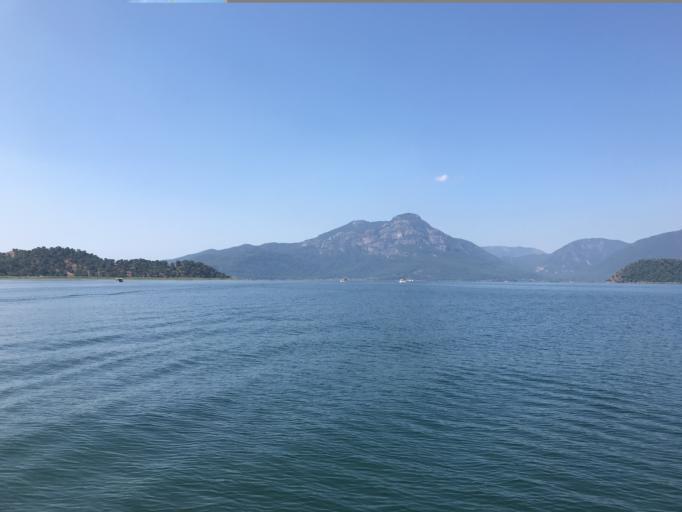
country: TR
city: Dalyan
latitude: 36.9091
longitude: 28.6519
